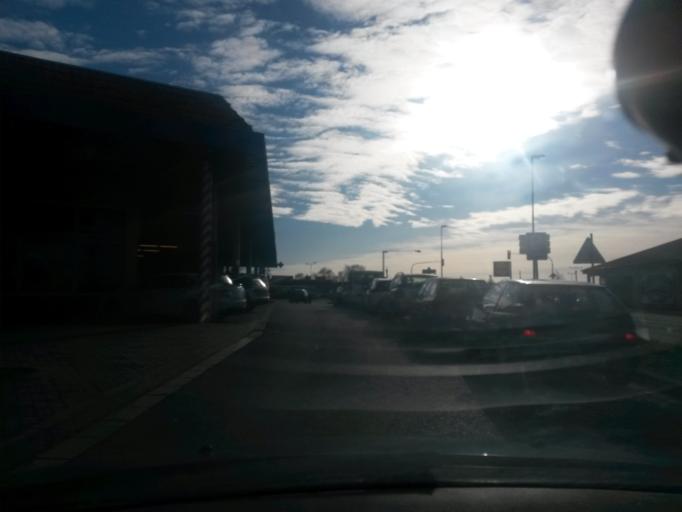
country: CZ
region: Central Bohemia
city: Jesenice
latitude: 49.9661
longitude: 14.5174
